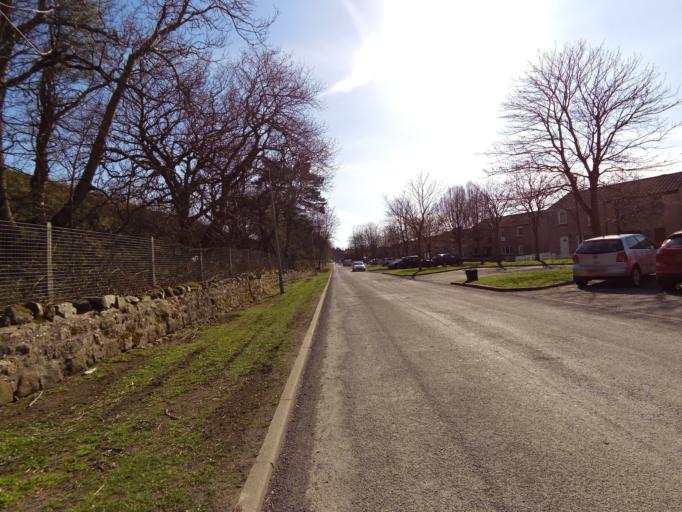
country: GB
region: Scotland
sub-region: Aberdeenshire
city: Portlethen
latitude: 57.0678
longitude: -2.1229
